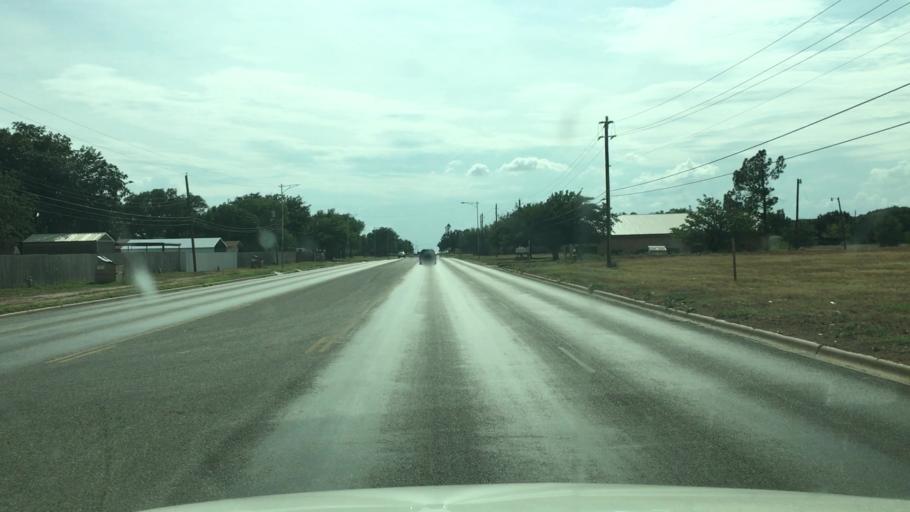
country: US
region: Texas
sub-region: Dawson County
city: Lamesa
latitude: 32.7534
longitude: -101.9579
